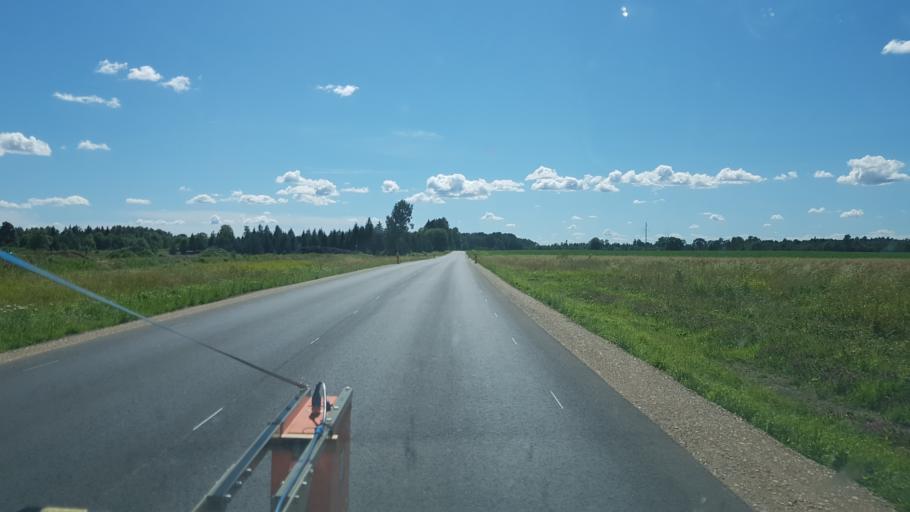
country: EE
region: Viljandimaa
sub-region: Karksi vald
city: Karksi-Nuia
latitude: 58.2031
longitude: 25.6195
